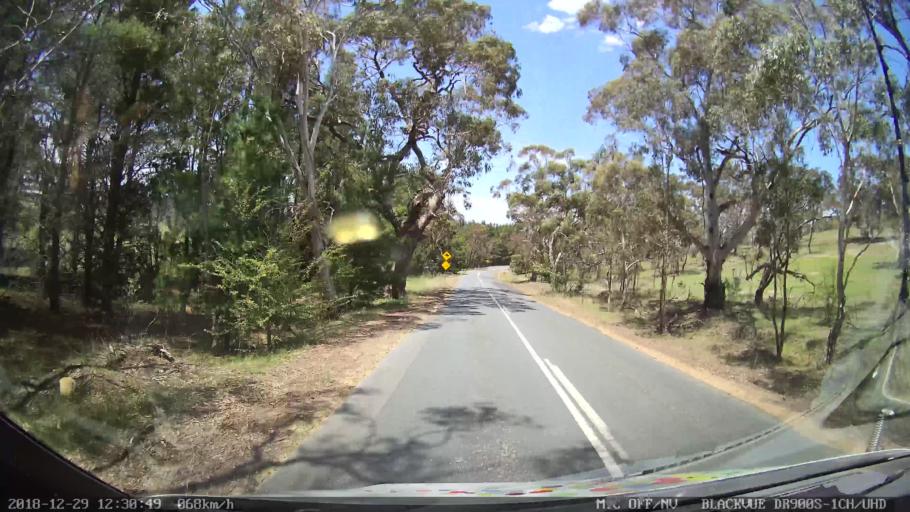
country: AU
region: Australian Capital Territory
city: Macarthur
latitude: -35.5094
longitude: 149.2329
